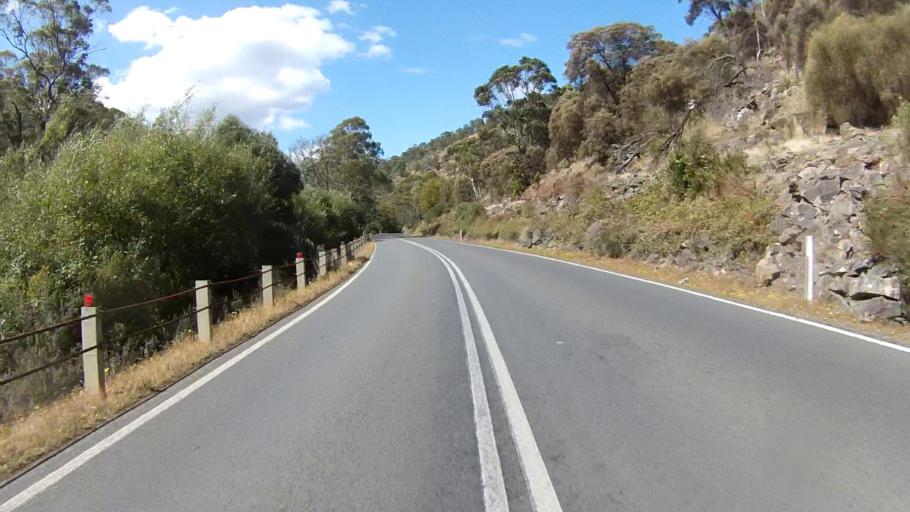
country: AU
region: Tasmania
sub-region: Derwent Valley
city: New Norfolk
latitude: -42.6815
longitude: 146.7666
